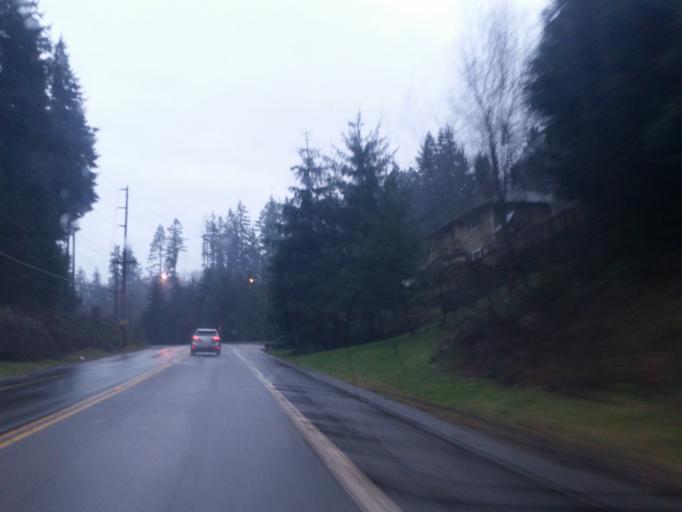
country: US
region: Washington
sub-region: Snohomish County
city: Meadowdale
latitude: 47.8755
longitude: -122.3126
